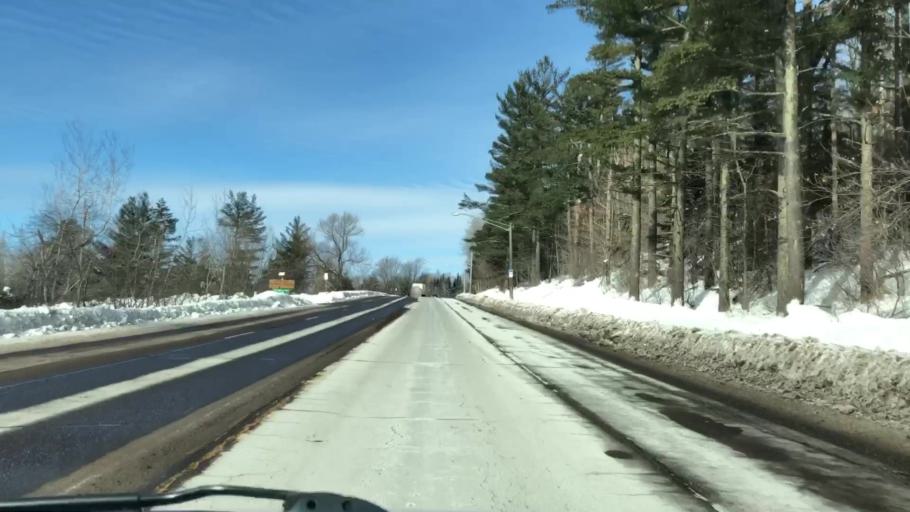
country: US
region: Minnesota
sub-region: Saint Louis County
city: Arnold
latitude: 46.8399
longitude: -92.0811
